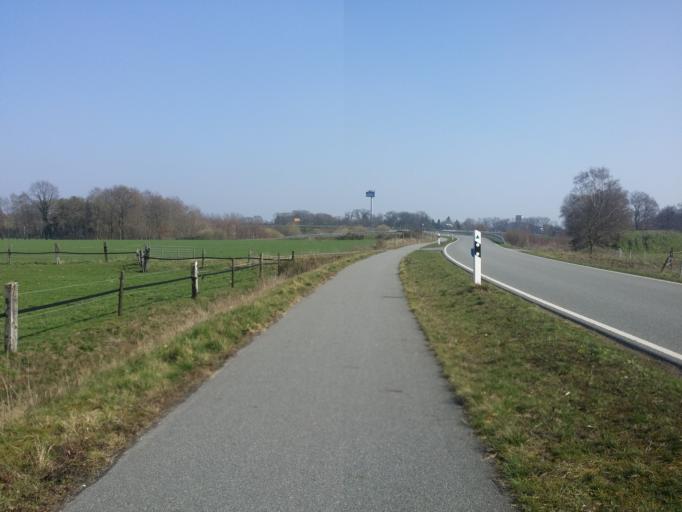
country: DE
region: Lower Saxony
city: Stuhr
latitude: 53.0140
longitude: 8.6901
